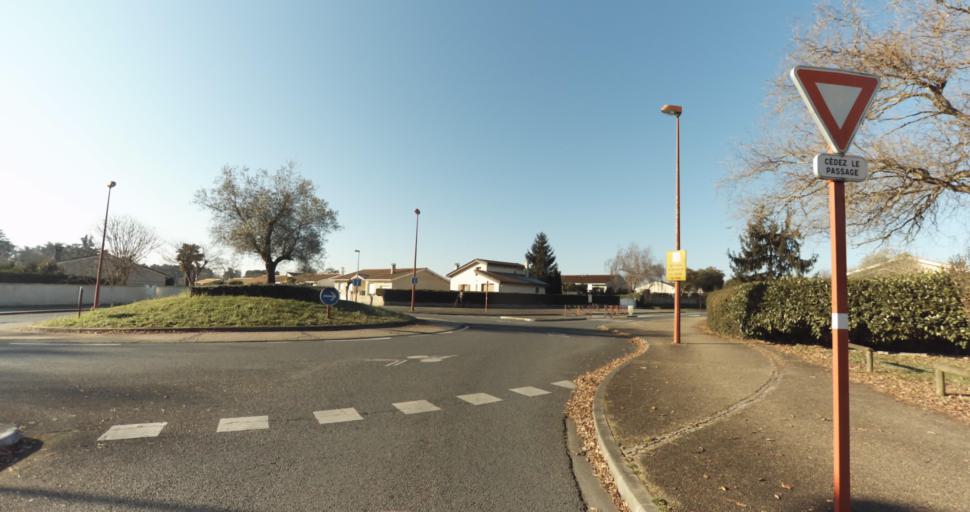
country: FR
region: Aquitaine
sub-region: Departement de la Gironde
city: Carbon-Blanc
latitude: 44.8882
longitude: -0.5111
